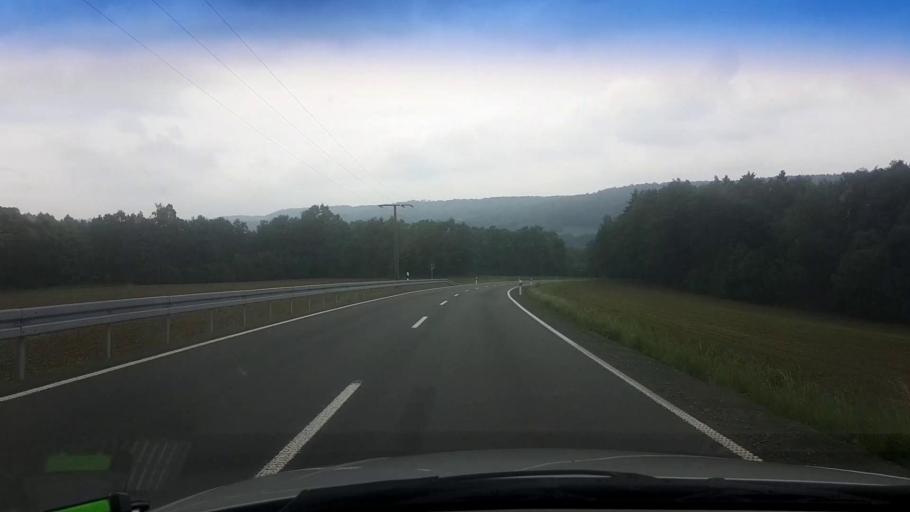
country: DE
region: Bavaria
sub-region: Upper Franconia
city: Reuth
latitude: 49.9770
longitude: 11.6959
